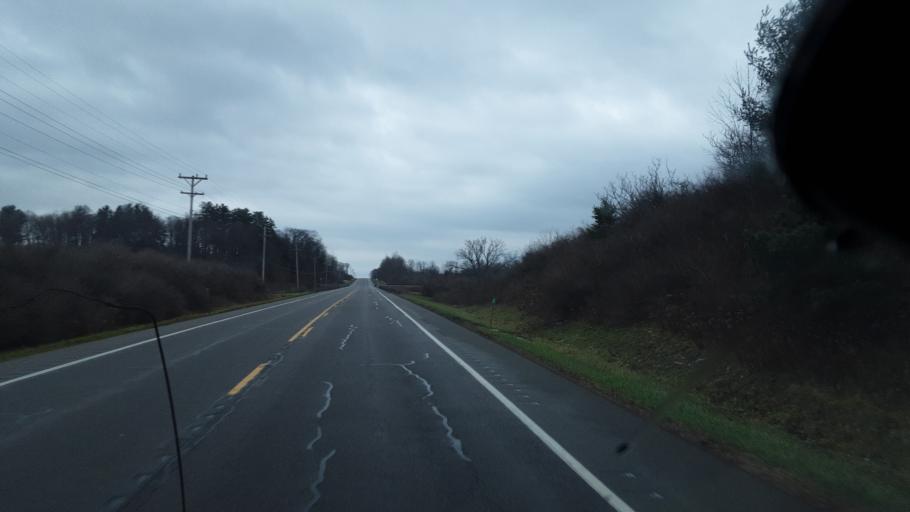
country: US
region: New York
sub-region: Allegany County
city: Houghton
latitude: 42.3910
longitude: -78.1955
